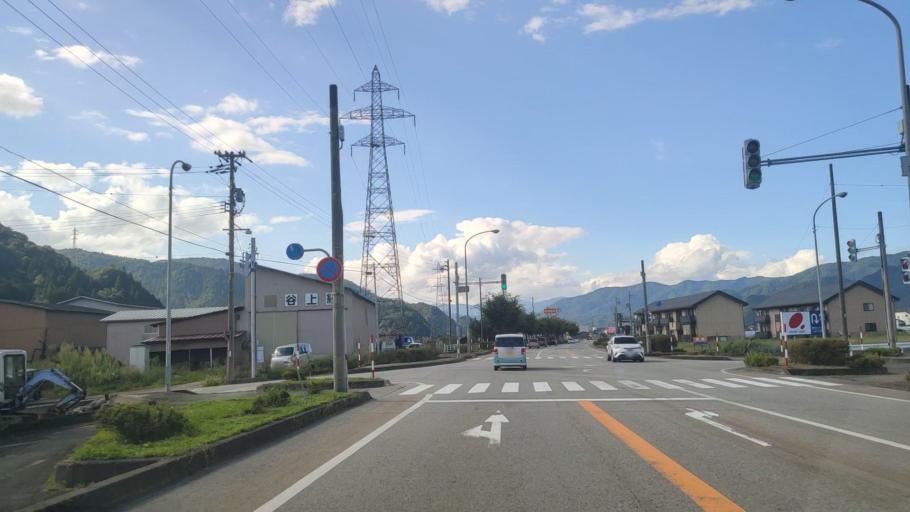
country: JP
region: Gifu
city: Takayama
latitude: 36.2225
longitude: 137.1909
